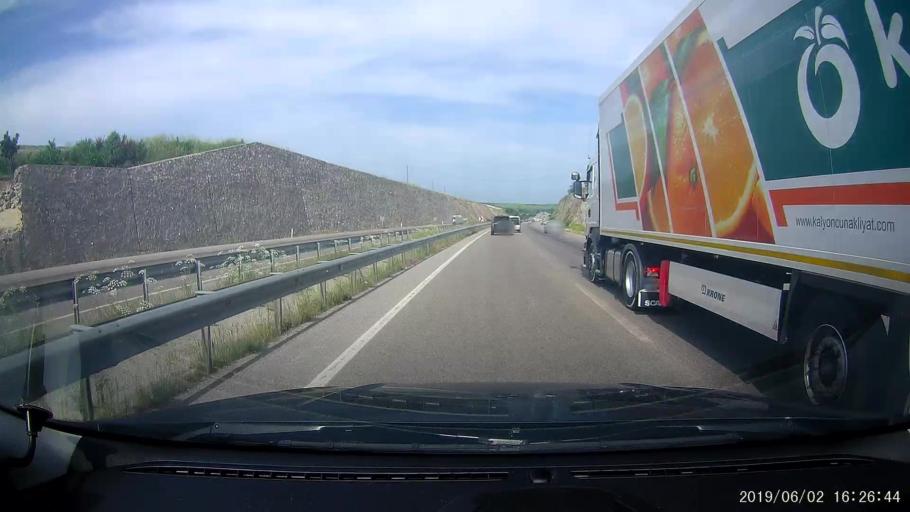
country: TR
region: Samsun
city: Ladik
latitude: 41.0012
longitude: 35.8100
